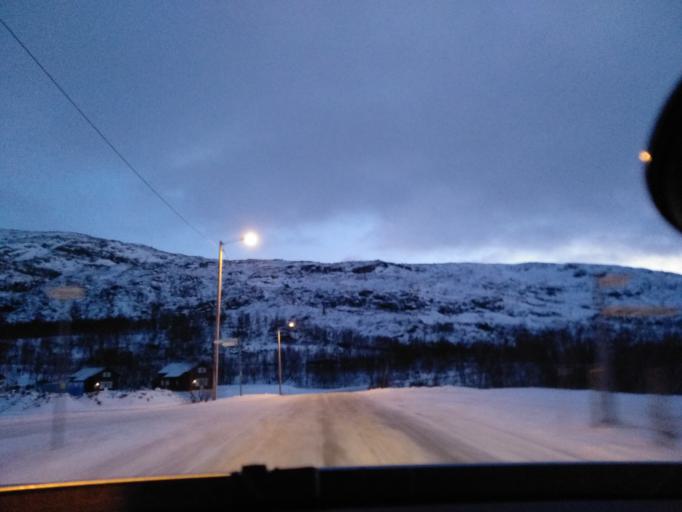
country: NO
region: Vest-Agder
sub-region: Sirdal
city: Tonstad
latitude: 59.0143
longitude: 6.9385
